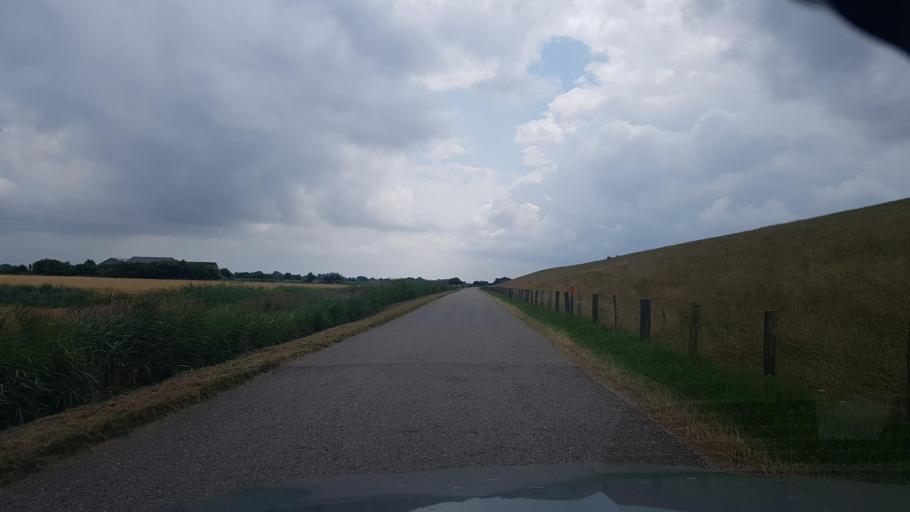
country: DE
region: Schleswig-Holstein
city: Elisabeth-Sophien-Koog
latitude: 54.4892
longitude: 8.8145
